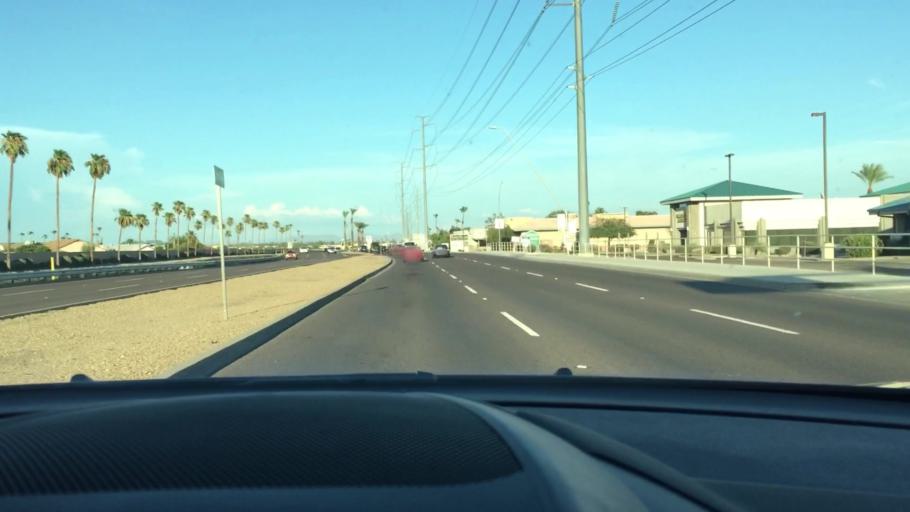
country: US
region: Arizona
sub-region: Maricopa County
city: Surprise
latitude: 33.6384
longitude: -112.3305
